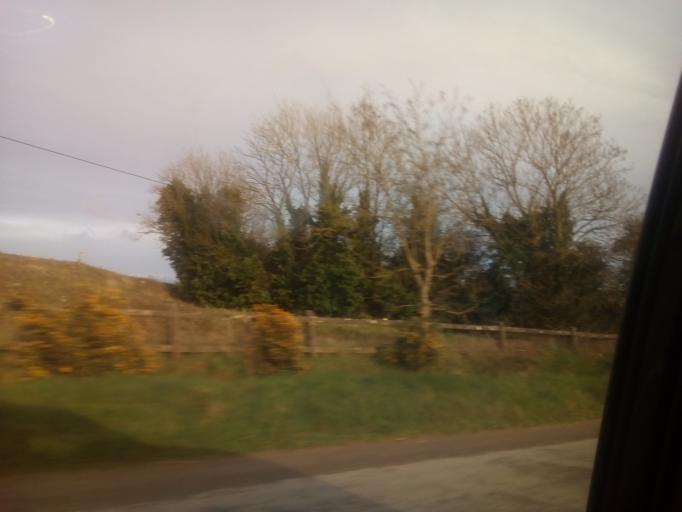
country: IE
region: Leinster
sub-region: Laois
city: Abbeyleix
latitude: 52.8761
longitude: -7.3621
